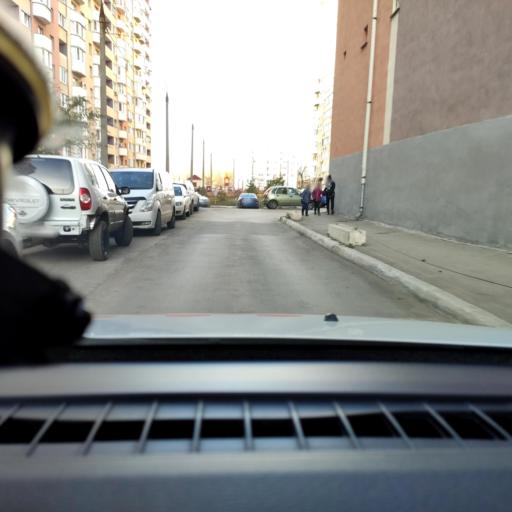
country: RU
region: Samara
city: Samara
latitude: 53.2469
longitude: 50.1918
